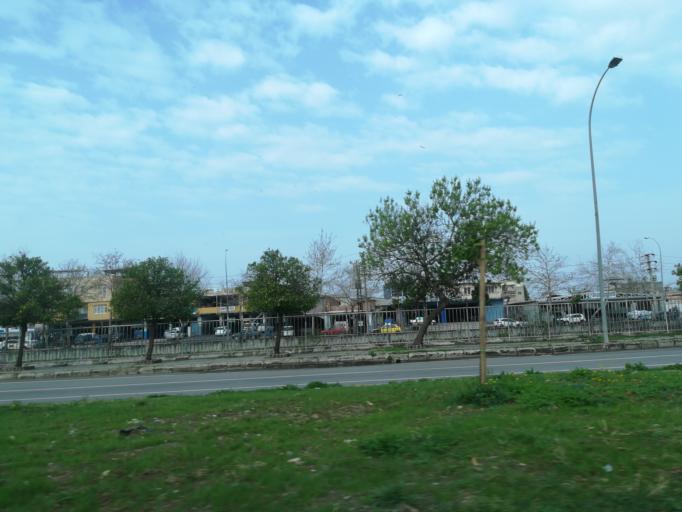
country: TR
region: Adana
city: Yuregir
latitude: 36.9860
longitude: 35.3677
